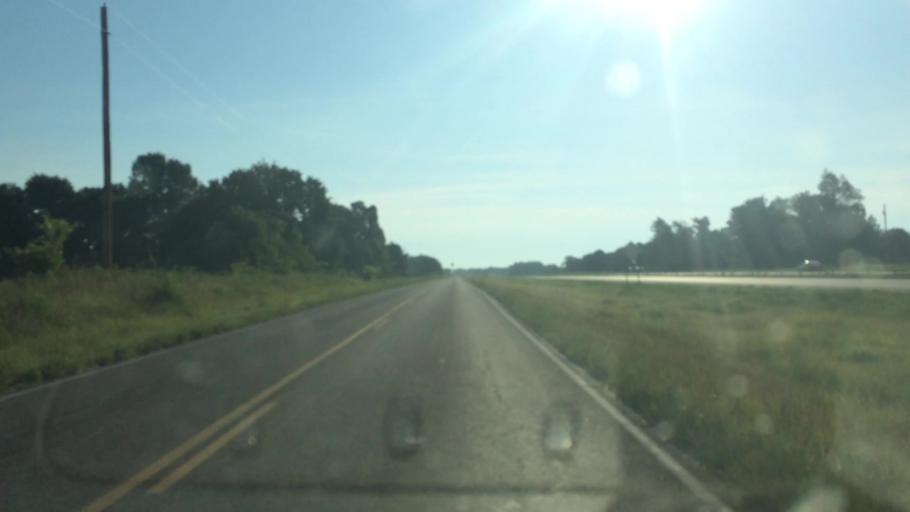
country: US
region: Missouri
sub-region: Greene County
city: Strafford
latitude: 37.2619
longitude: -93.1501
